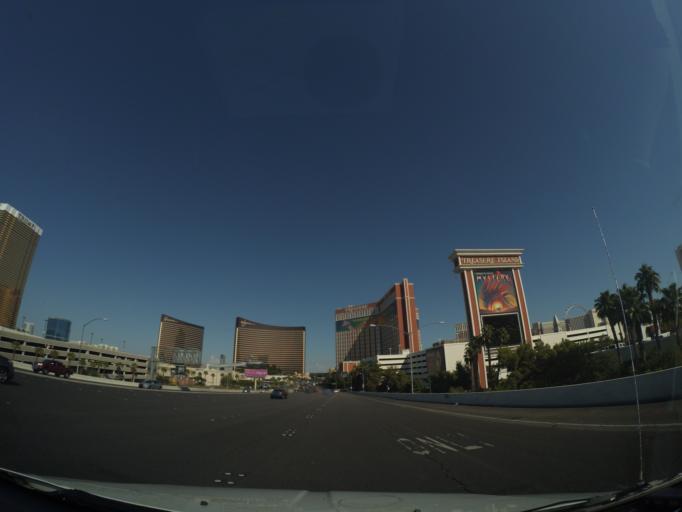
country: US
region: Nevada
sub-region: Clark County
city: Paradise
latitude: 36.1258
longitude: -115.1762
